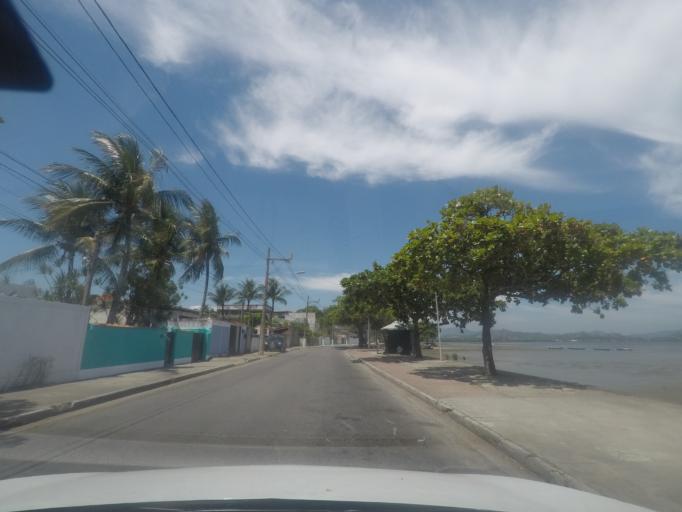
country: BR
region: Rio de Janeiro
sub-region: Itaguai
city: Itaguai
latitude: -22.9851
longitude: -43.6863
